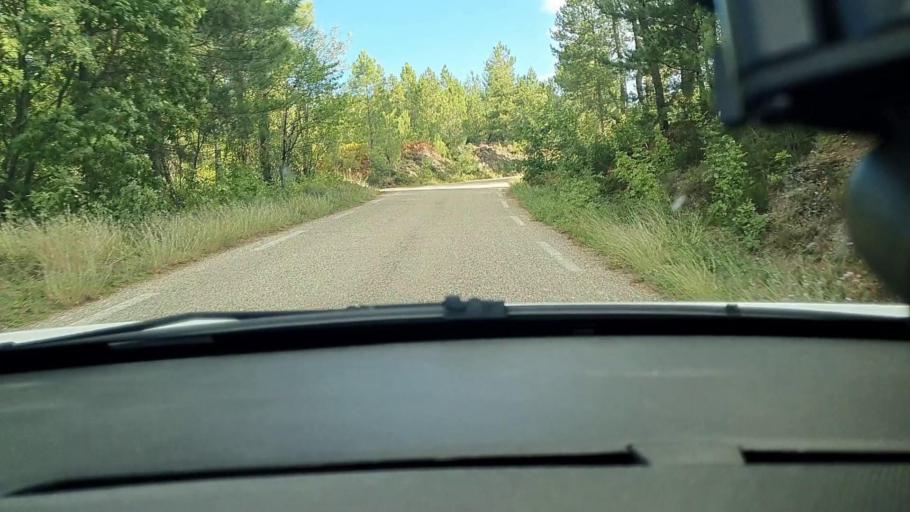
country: FR
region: Languedoc-Roussillon
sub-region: Departement du Gard
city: Besseges
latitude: 44.3479
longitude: 3.9813
